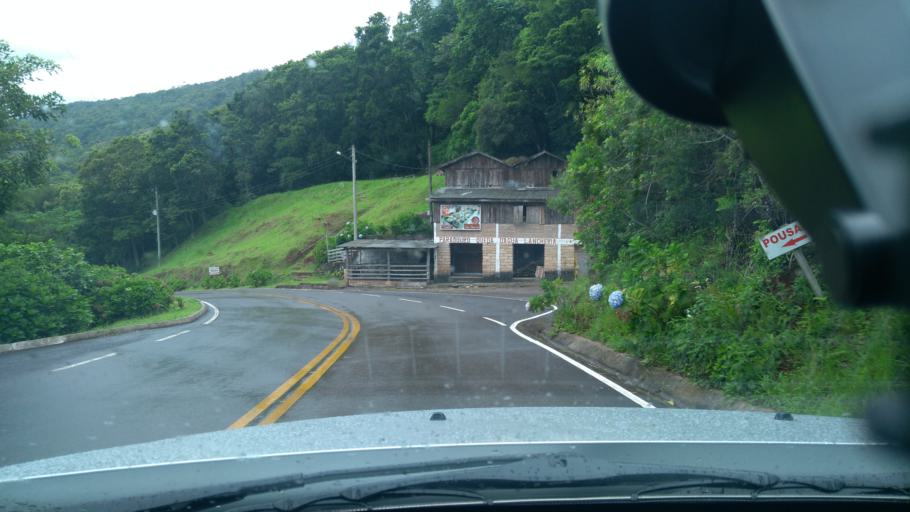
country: BR
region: Rio Grande do Sul
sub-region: Torres
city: Torres
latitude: -29.1860
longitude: -49.9882
